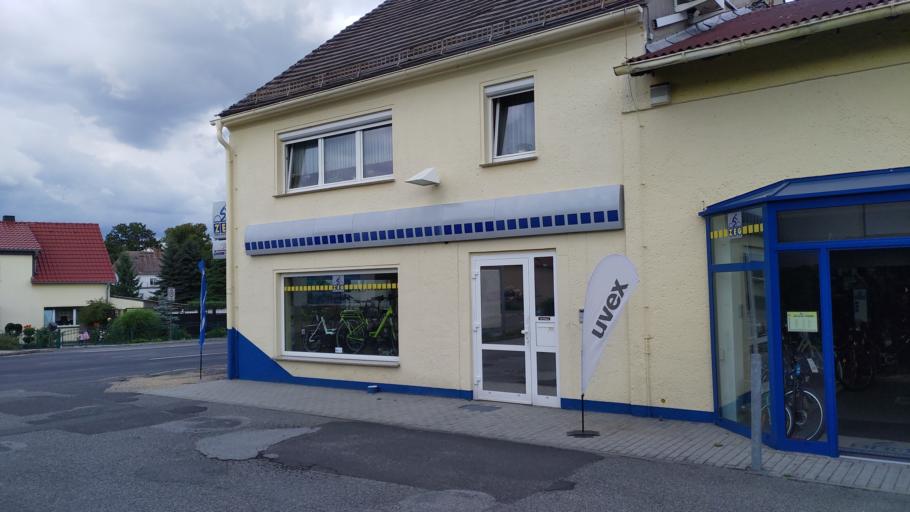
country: DE
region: Saxony
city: Niesky
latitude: 51.2917
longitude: 14.8345
